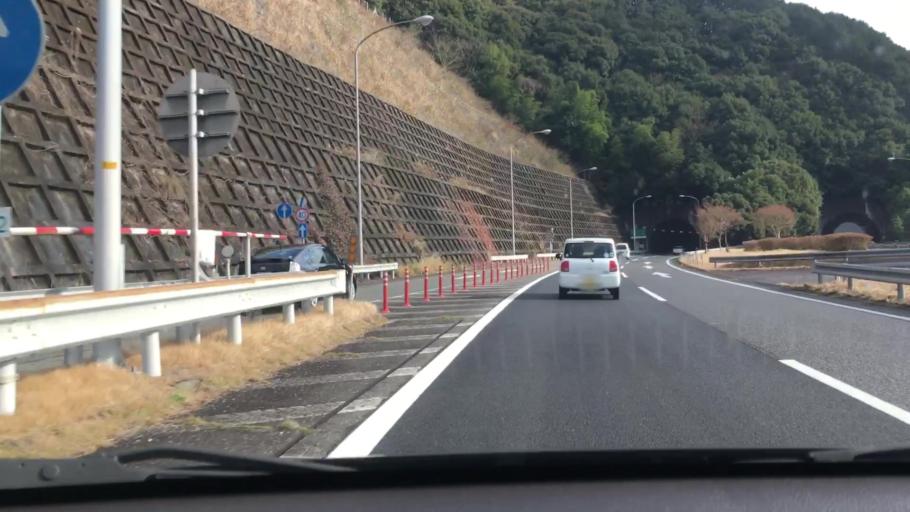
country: JP
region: Kumamoto
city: Yatsushiro
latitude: 32.4419
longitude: 130.6699
